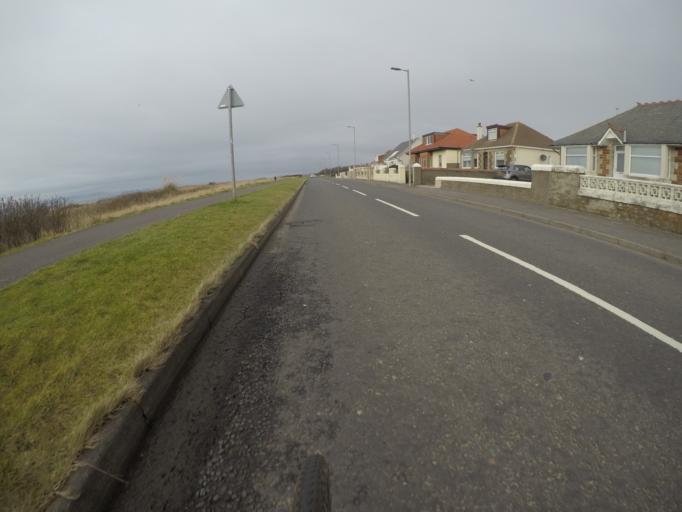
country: GB
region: Scotland
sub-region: North Ayrshire
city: Ardrossan
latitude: 55.6500
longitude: -4.8164
